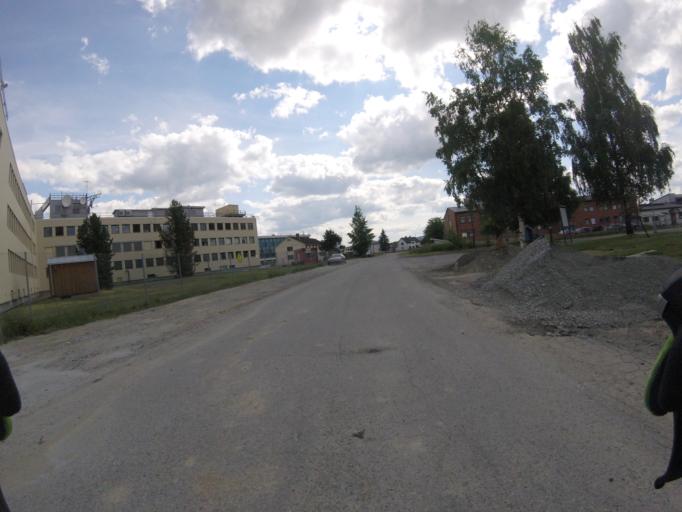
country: NO
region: Akershus
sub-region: Skedsmo
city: Lillestrom
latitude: 59.9752
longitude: 11.0459
